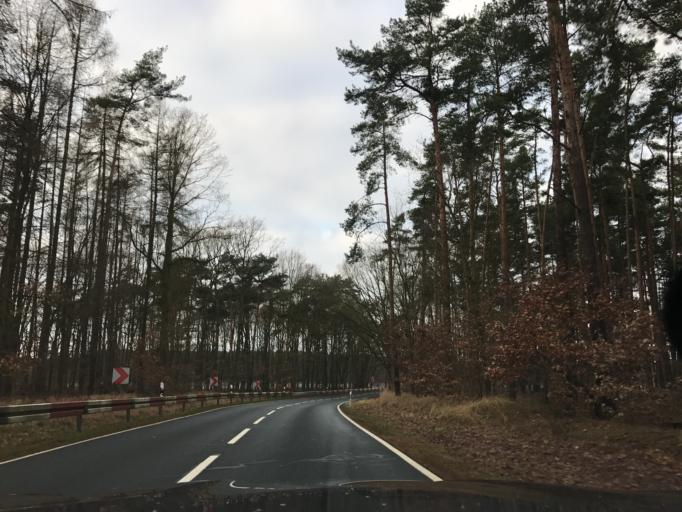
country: DE
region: Brandenburg
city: Gross Kreutz
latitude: 52.3352
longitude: 12.7117
